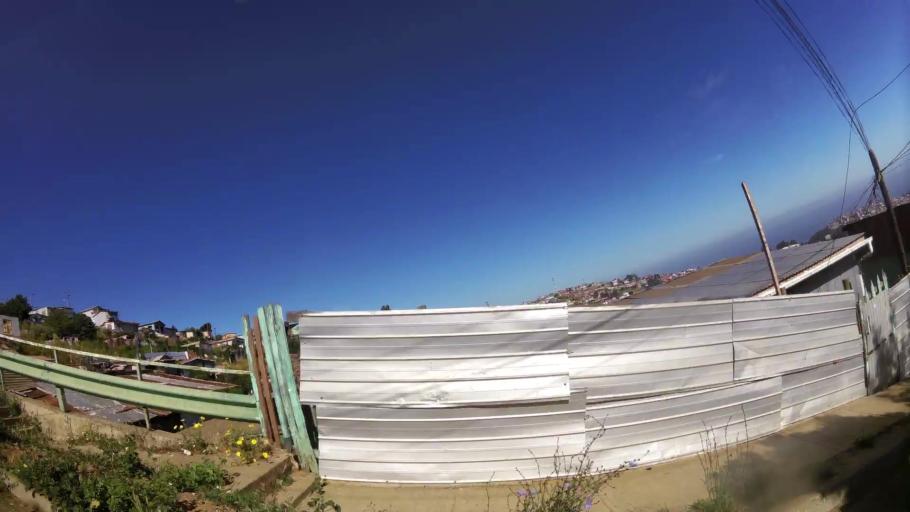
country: CL
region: Valparaiso
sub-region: Provincia de Valparaiso
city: Valparaiso
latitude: -33.0531
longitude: -71.6393
